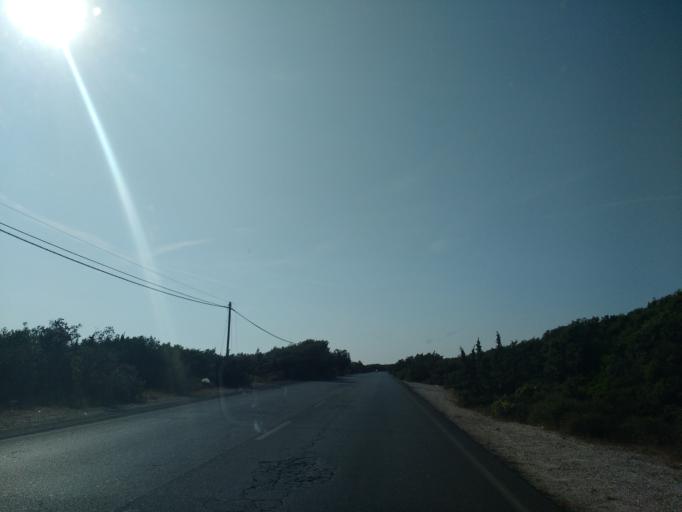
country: IT
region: Latium
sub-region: Citta metropolitana di Roma Capitale
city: Acilia-Castel Fusano-Ostia Antica
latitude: 41.6882
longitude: 12.3726
